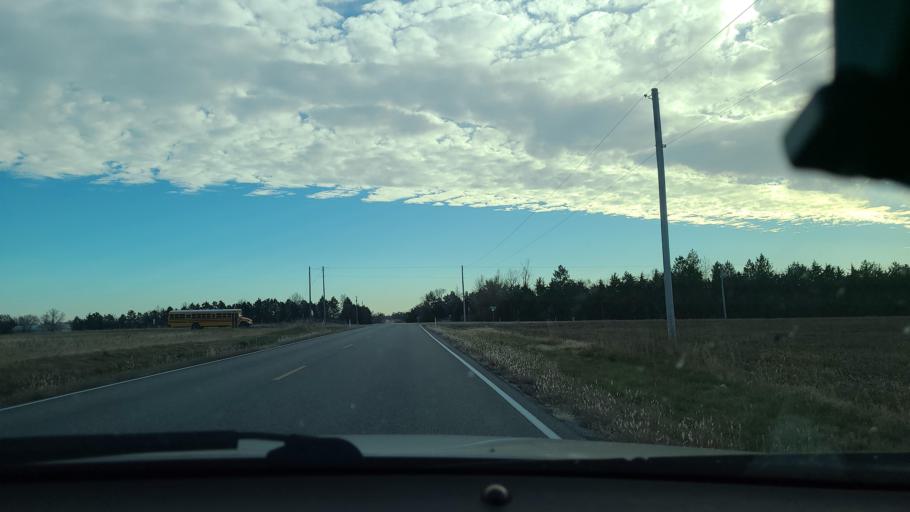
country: US
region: Kansas
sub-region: Sedgwick County
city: Goddard
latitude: 37.6504
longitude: -97.5891
